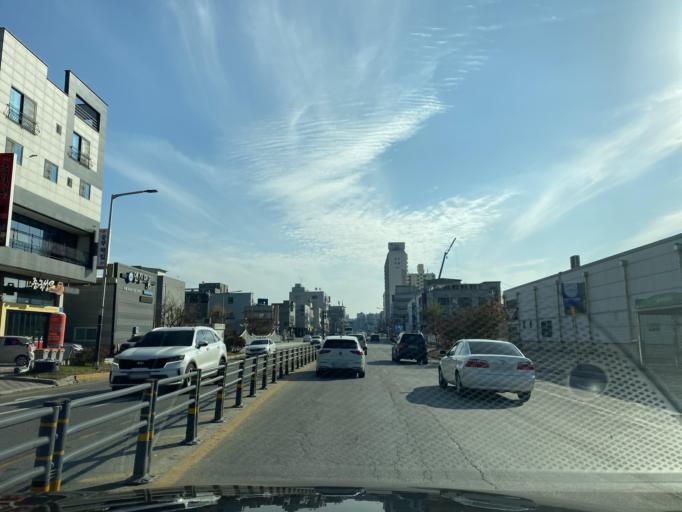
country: KR
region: Chungcheongnam-do
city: Cheonan
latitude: 36.8057
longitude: 127.1587
